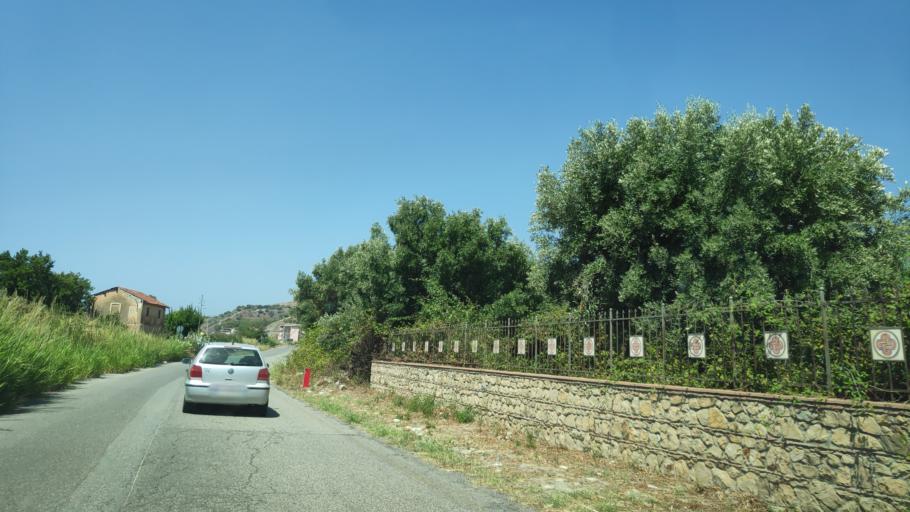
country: IT
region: Calabria
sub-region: Provincia di Reggio Calabria
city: Palizzi Marina
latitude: 37.9231
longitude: 15.9533
